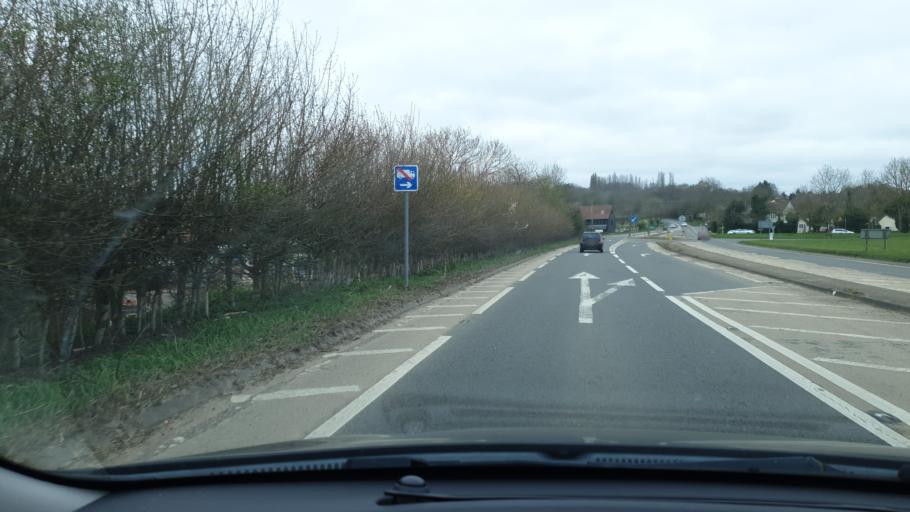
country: GB
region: England
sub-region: Essex
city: Great Horkesley
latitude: 51.9704
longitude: 0.8646
